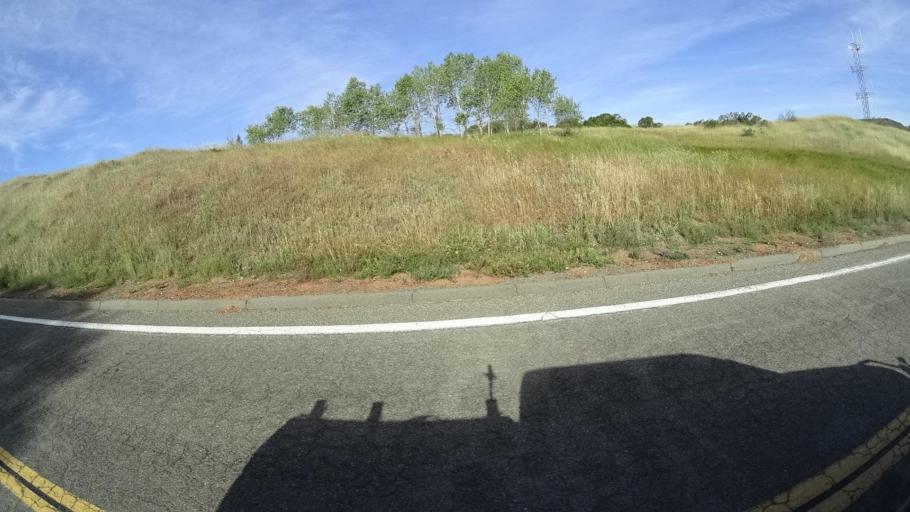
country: US
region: California
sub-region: Lake County
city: North Lakeport
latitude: 39.1016
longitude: -122.9137
